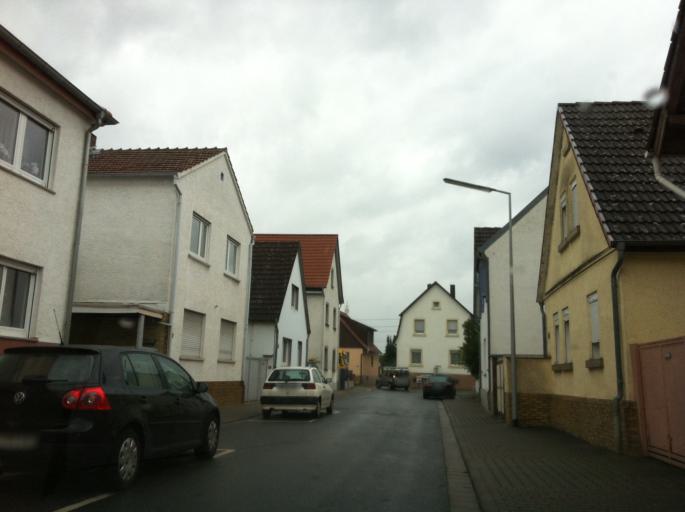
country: DE
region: Hesse
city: Weiterstadt
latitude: 49.9074
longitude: 8.5867
